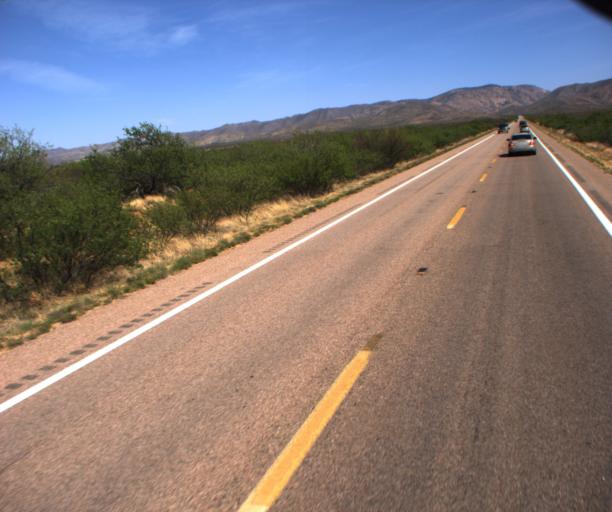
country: US
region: Arizona
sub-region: Cochise County
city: Bisbee
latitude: 31.5371
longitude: -110.0675
